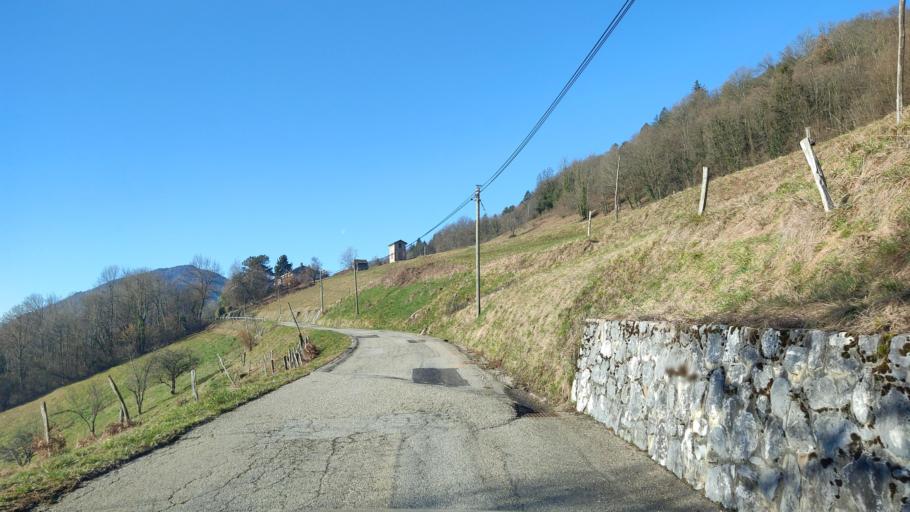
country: FR
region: Rhone-Alpes
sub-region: Departement de la Savoie
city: La Rochette
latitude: 45.4649
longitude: 6.1095
